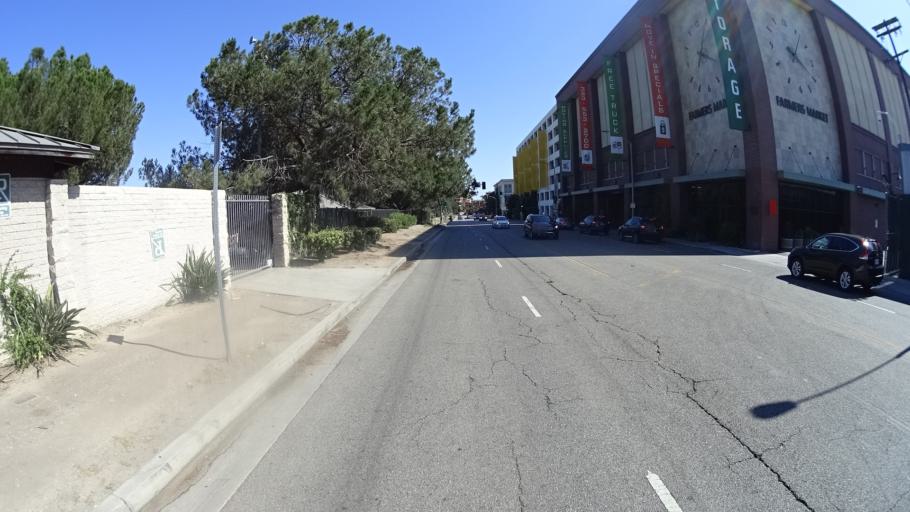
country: US
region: California
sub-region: Los Angeles County
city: West Hollywood
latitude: 34.0738
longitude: -118.3564
